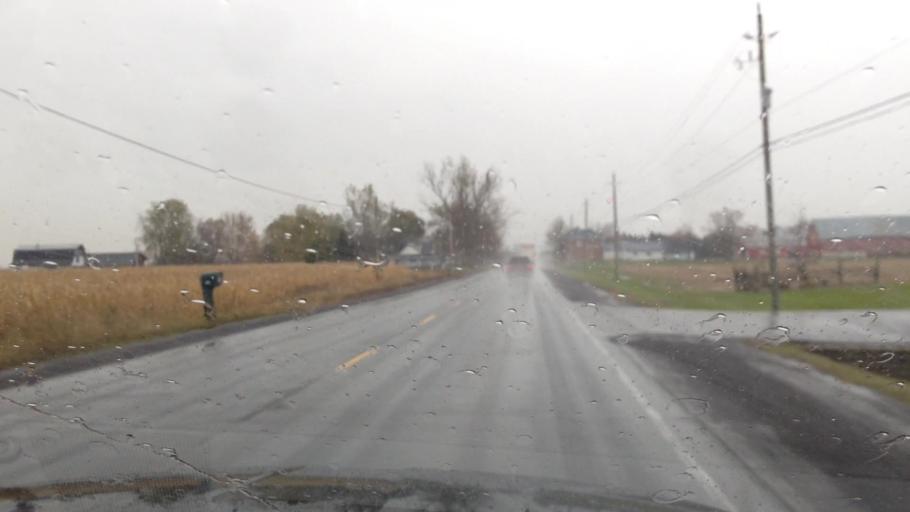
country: CA
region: Ontario
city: Bourget
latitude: 45.2945
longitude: -75.3250
